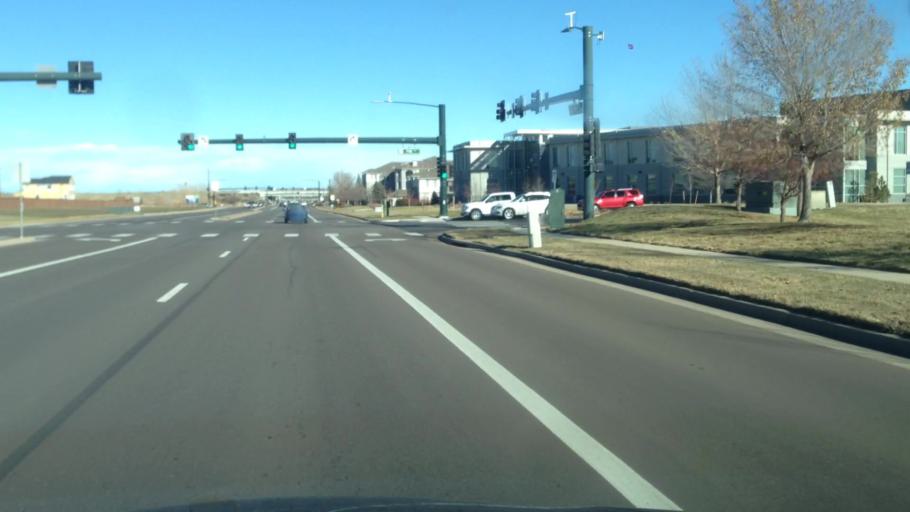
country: US
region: Colorado
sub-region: Douglas County
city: Stonegate
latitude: 39.5426
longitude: -104.7934
